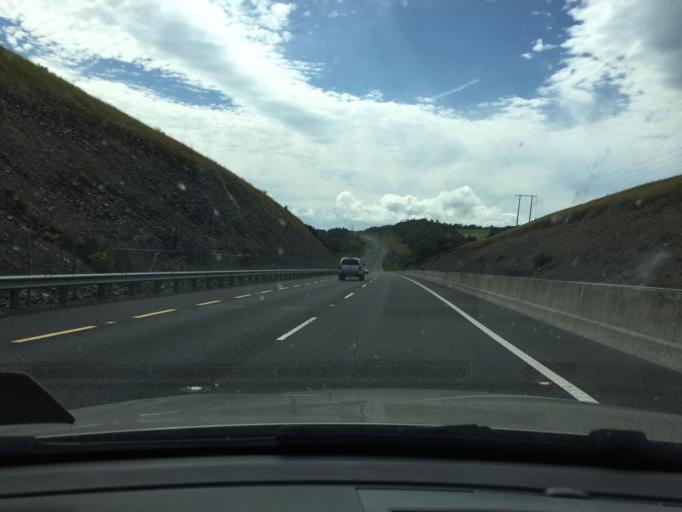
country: IE
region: Leinster
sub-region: Kilkenny
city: Mooncoin
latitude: 52.2366
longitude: -7.2042
